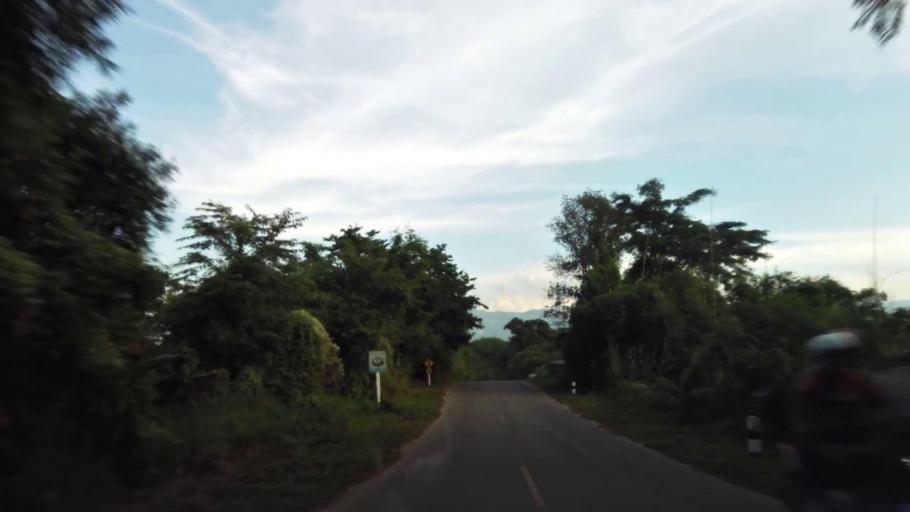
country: TH
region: Chiang Rai
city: Khun Tan
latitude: 19.8729
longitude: 100.3461
